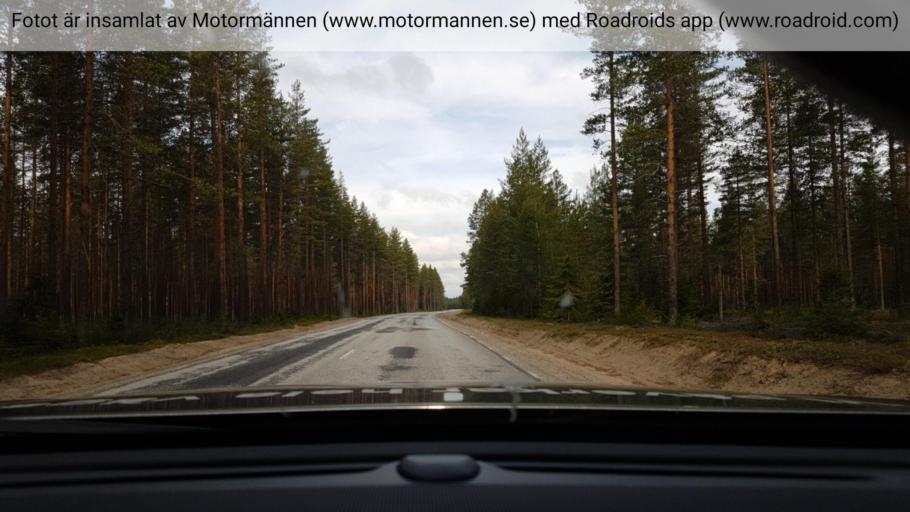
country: SE
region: Vaesterbotten
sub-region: Vindelns Kommun
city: Vindeln
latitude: 64.1678
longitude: 19.7787
